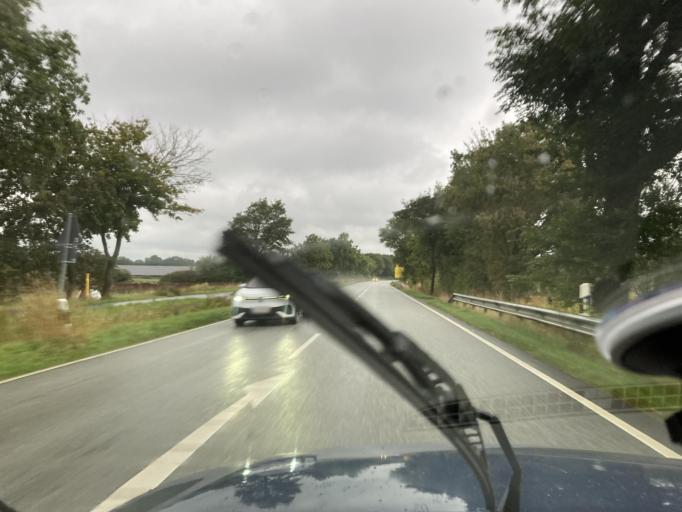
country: DE
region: Schleswig-Holstein
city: Welmbuttel
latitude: 54.2081
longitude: 9.2664
